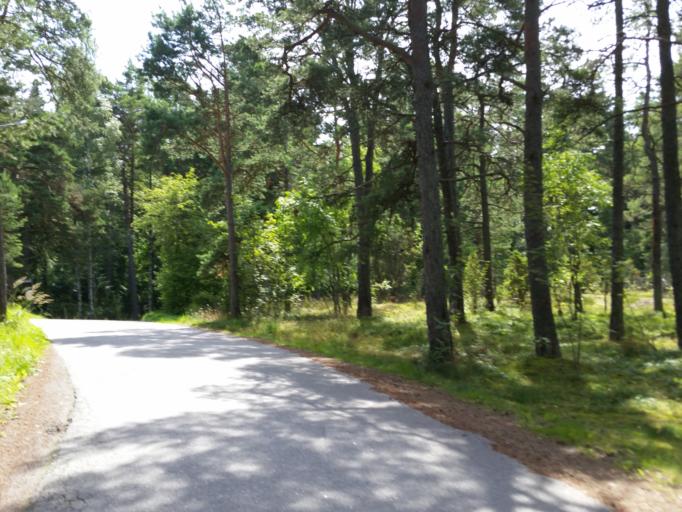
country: FI
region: Uusimaa
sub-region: Raaseporin
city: Hanko
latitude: 59.8438
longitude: 22.9421
